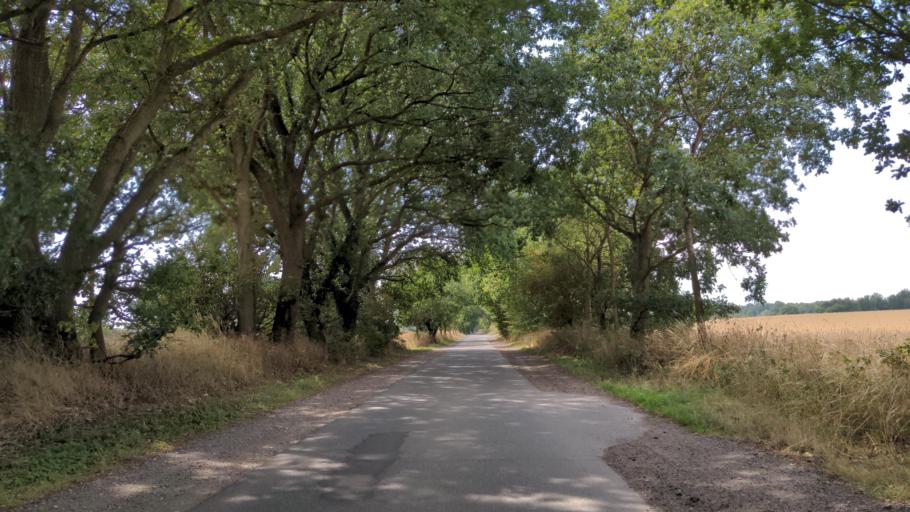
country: DE
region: Schleswig-Holstein
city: Gross Gronau
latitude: 53.8413
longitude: 10.7810
